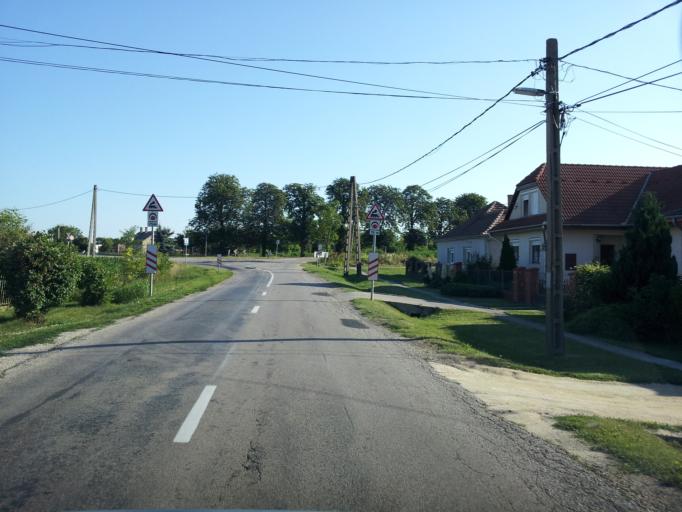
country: HU
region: Fejer
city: Polgardi
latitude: 47.0681
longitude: 18.2824
